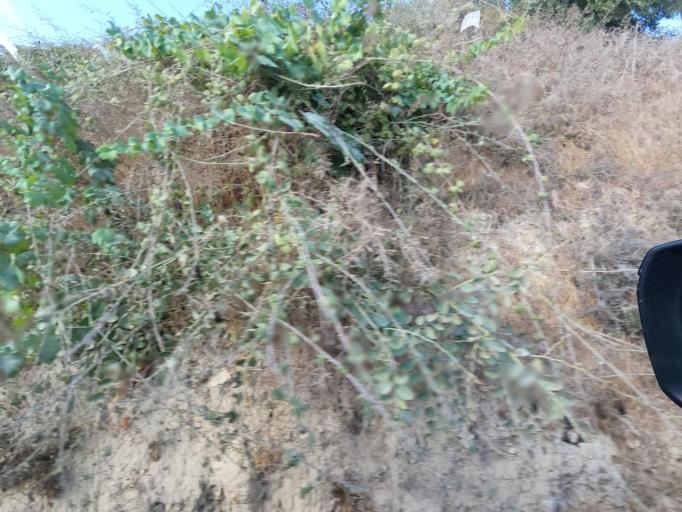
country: CY
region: Pafos
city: Mesogi
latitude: 34.8439
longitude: 32.5247
